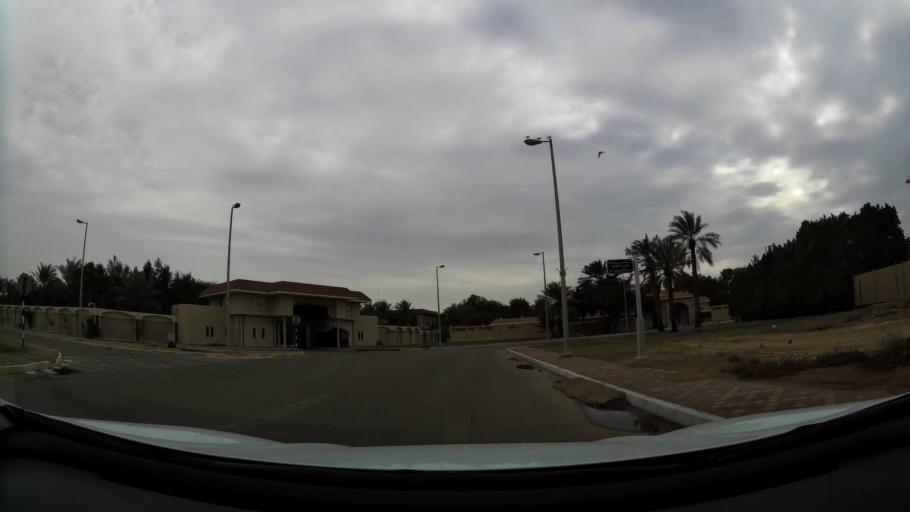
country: AE
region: Abu Dhabi
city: Abu Dhabi
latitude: 24.4119
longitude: 54.4264
